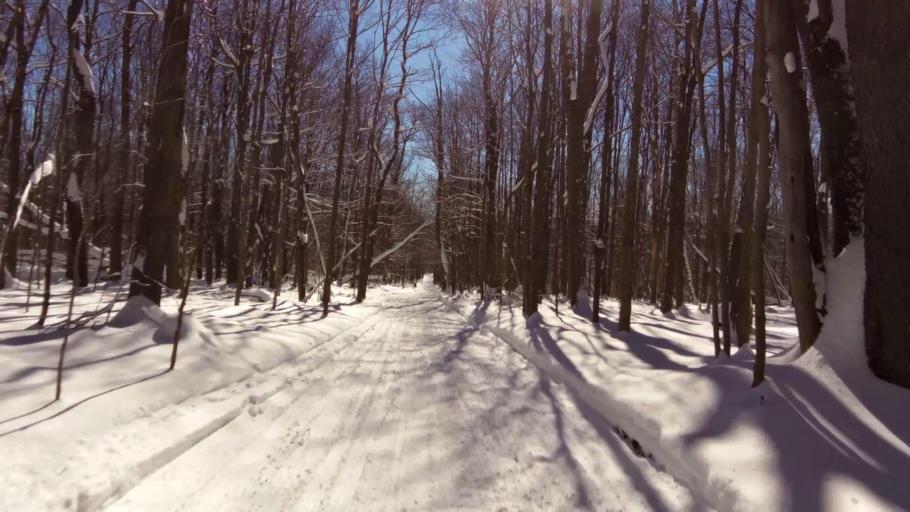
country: US
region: New York
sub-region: Chautauqua County
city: Mayville
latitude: 42.2093
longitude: -79.5348
